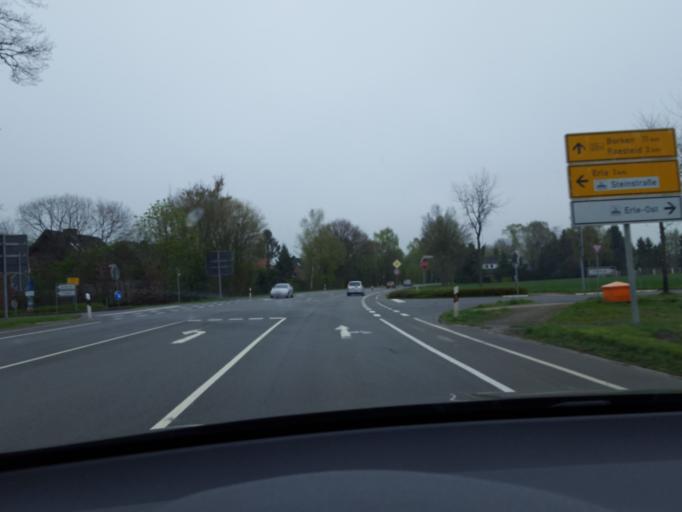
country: DE
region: North Rhine-Westphalia
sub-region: Regierungsbezirk Munster
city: Raesfeld
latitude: 51.7444
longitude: 6.8715
